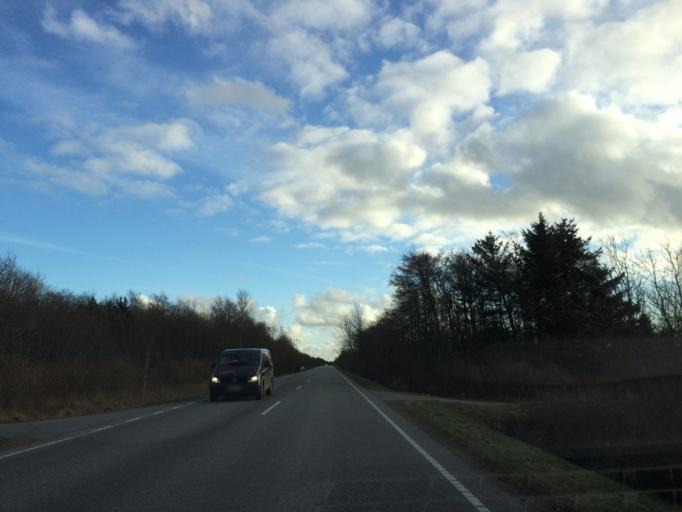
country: DK
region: Central Jutland
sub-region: Holstebro Kommune
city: Ulfborg
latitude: 56.3788
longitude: 8.3284
